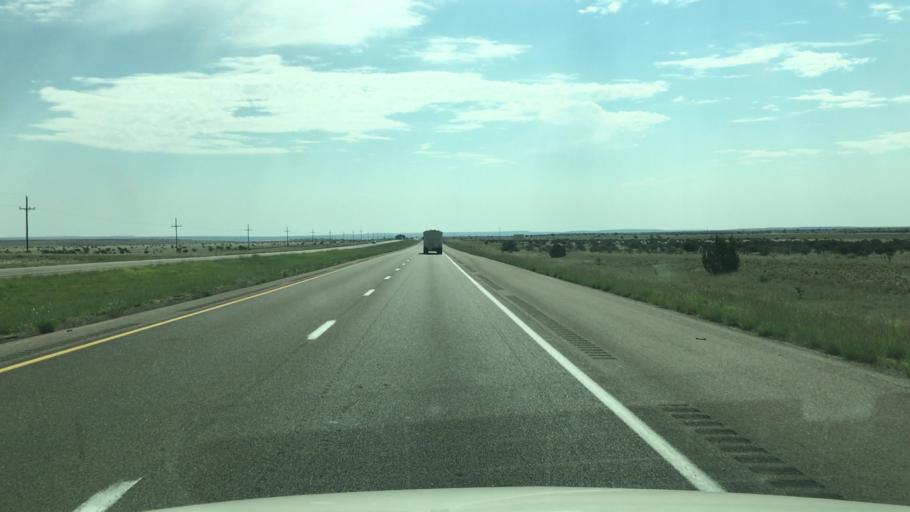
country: US
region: New Mexico
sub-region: Guadalupe County
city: Santa Rosa
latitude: 34.9829
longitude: -105.1214
